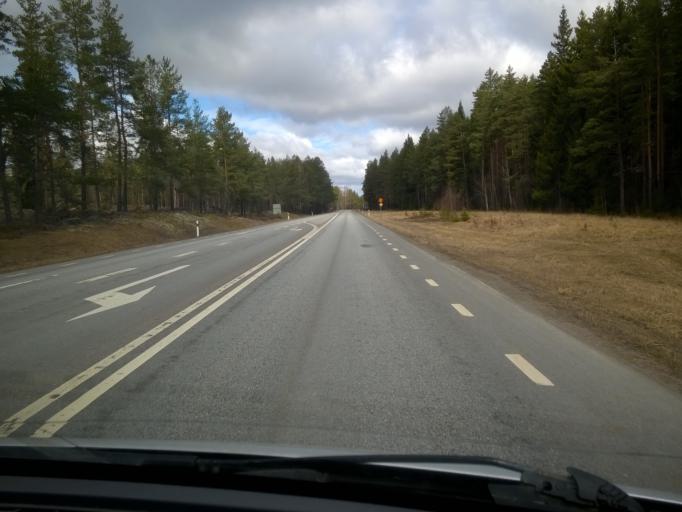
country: SE
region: Uppsala
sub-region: Tierps Kommun
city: Tierp
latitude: 60.1839
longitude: 17.4787
